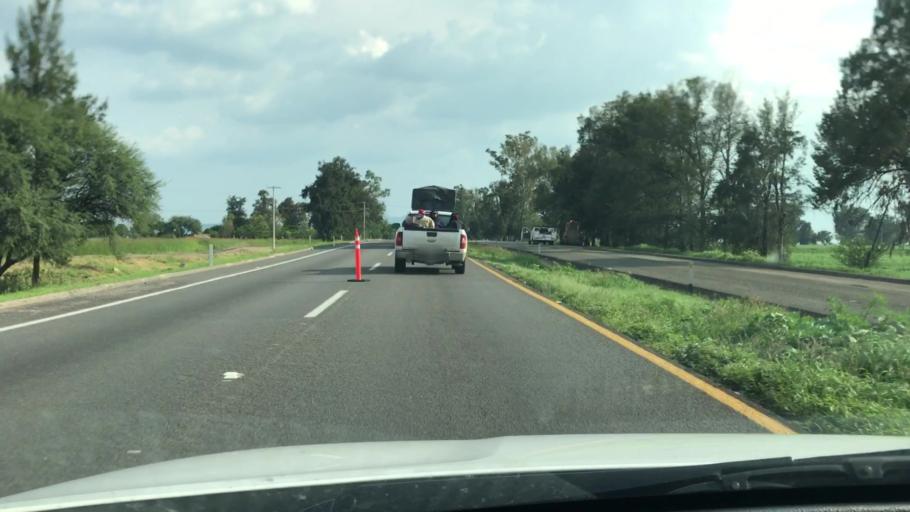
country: MX
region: Guanajuato
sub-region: Irapuato
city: San Ignacio de Rivera (Ojo de Agua)
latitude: 20.5239
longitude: -101.4628
